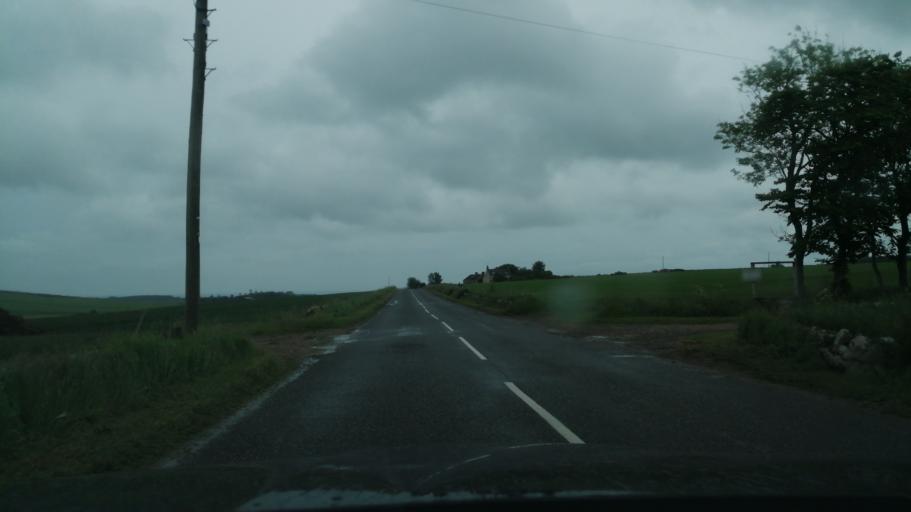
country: GB
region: Scotland
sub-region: Aberdeenshire
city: Portsoy
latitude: 57.6448
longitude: -2.7109
